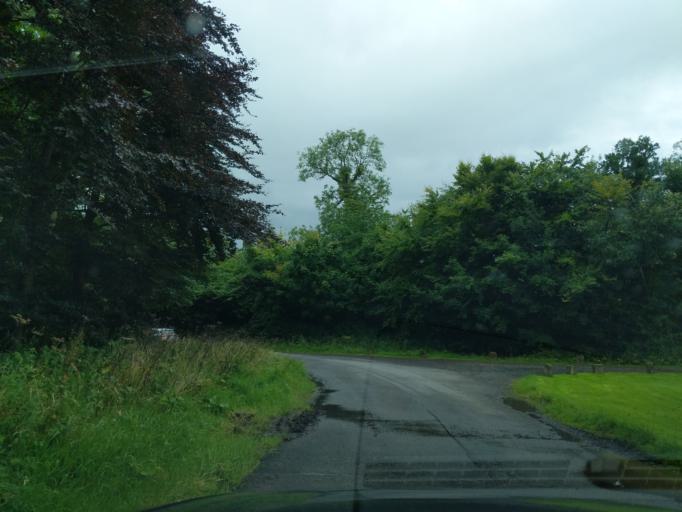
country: GB
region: Scotland
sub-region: Fife
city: Limekilns
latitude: 55.9926
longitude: -3.4797
